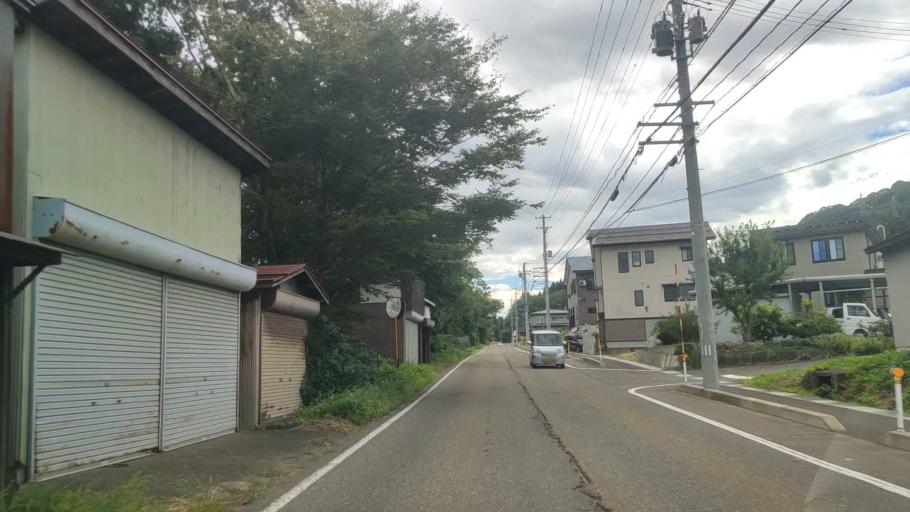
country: JP
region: Niigata
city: Arai
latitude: 37.0003
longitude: 138.2654
